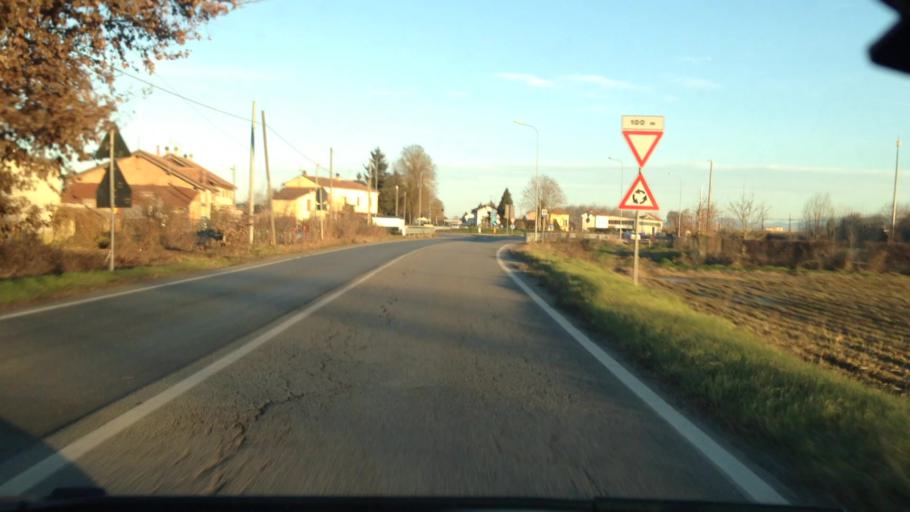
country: IT
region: Piedmont
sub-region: Provincia di Alessandria
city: Solero
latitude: 44.9215
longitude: 8.5587
